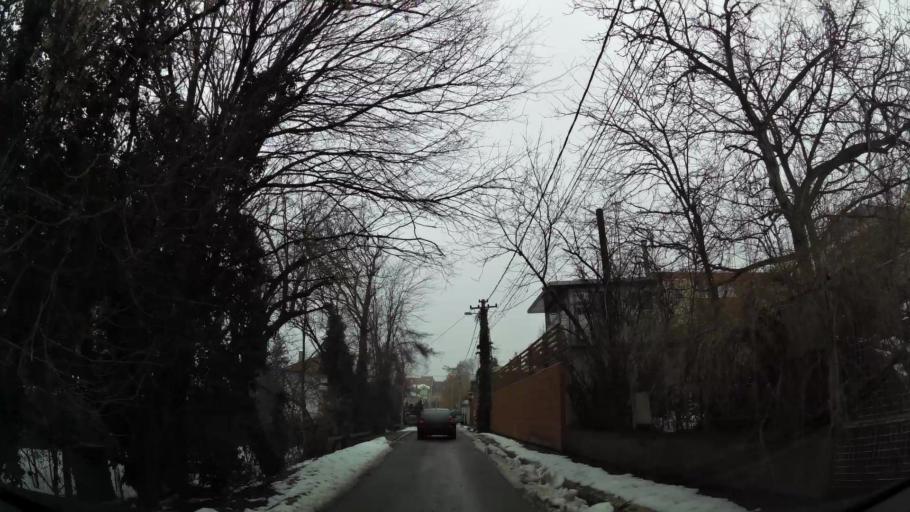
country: RS
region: Central Serbia
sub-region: Belgrade
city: Savski Venac
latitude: 44.7825
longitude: 20.4492
